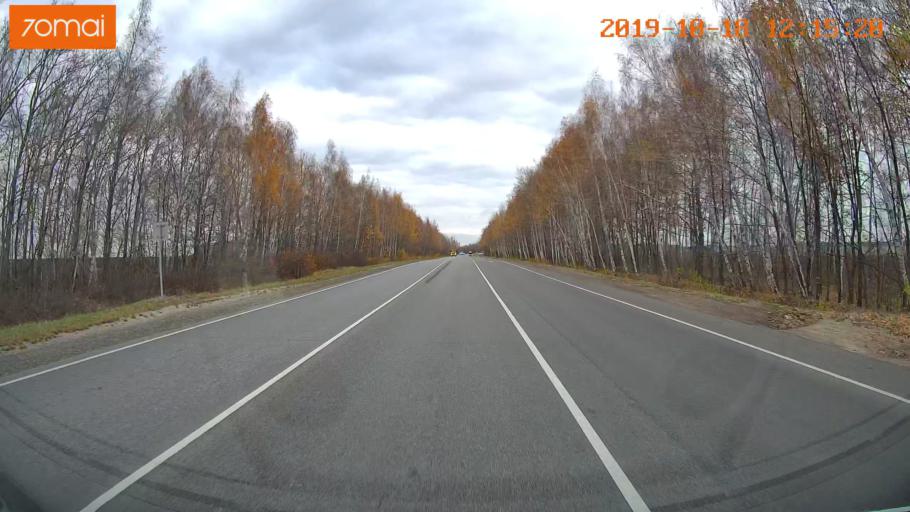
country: RU
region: Rjazan
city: Zakharovo
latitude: 54.4421
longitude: 39.3984
